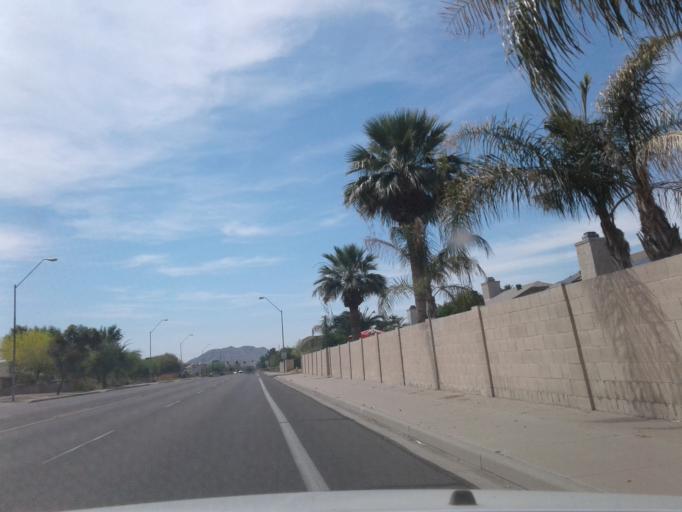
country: US
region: Arizona
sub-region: Maricopa County
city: Paradise Valley
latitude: 33.6294
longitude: -111.9962
